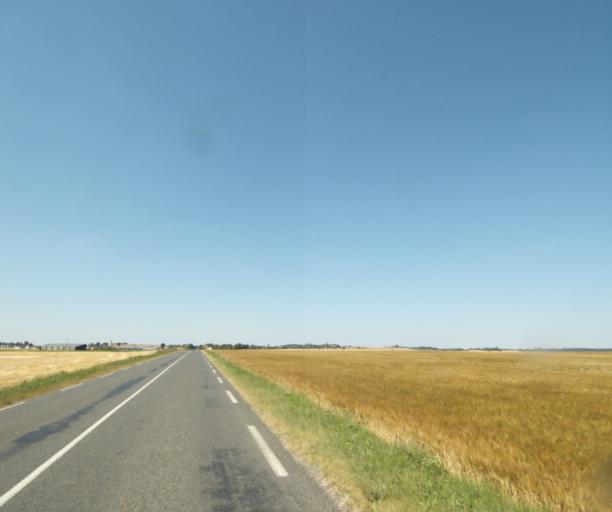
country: FR
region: Ile-de-France
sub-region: Departement de Seine-et-Marne
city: La Chapelle-la-Reine
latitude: 48.3030
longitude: 2.5735
